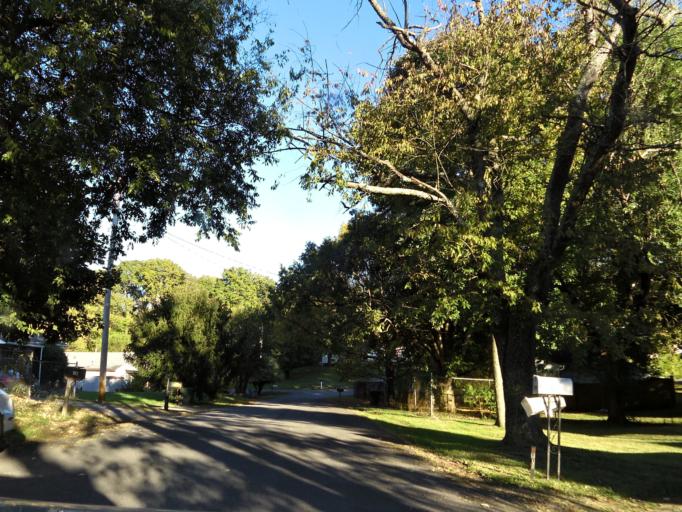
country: US
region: Tennessee
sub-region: Blount County
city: Alcoa
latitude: 35.7887
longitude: -83.9528
